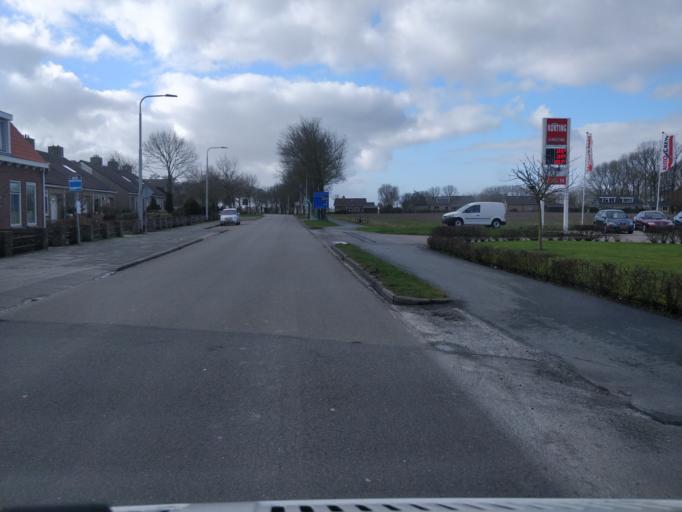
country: NL
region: Friesland
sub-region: Gemeente Franekeradeel
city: Sexbierum
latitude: 53.2214
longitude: 5.4851
